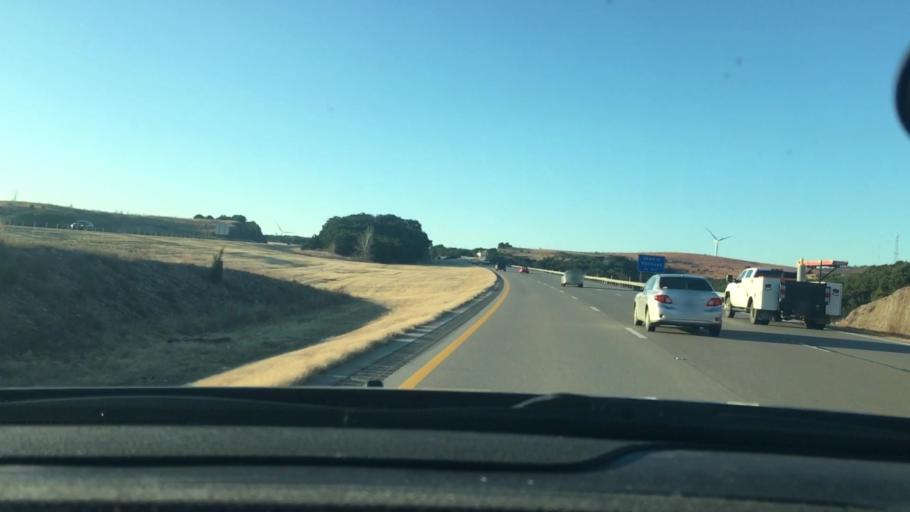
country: US
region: Oklahoma
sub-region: Murray County
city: Davis
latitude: 34.4322
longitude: -97.1322
